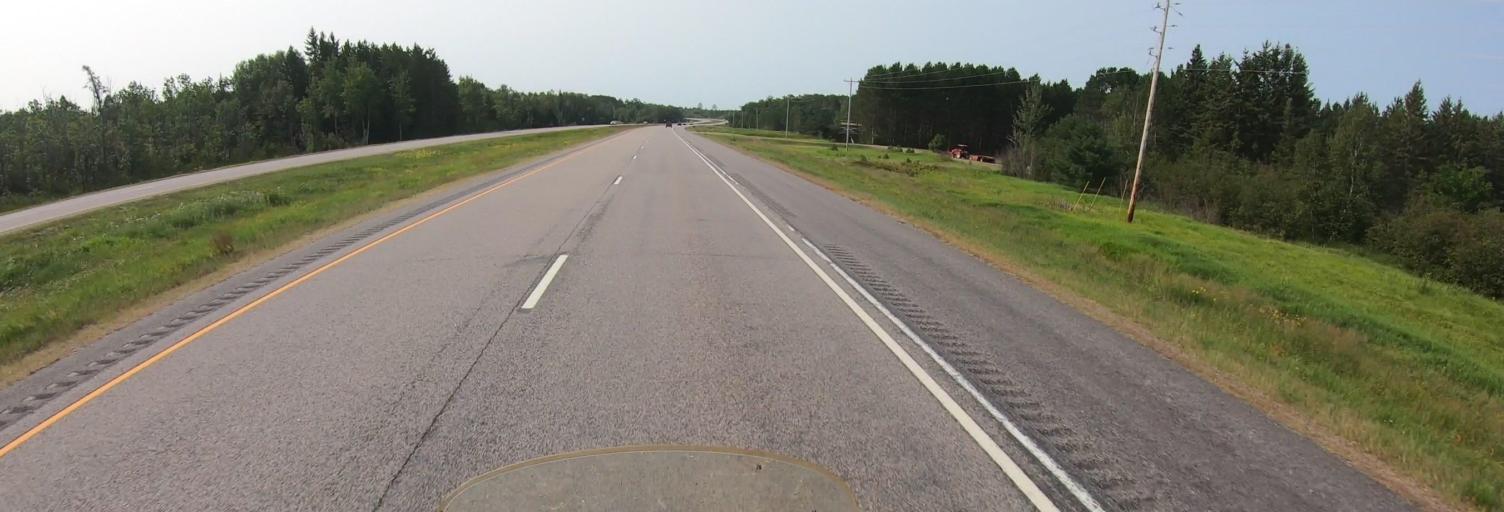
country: US
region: Minnesota
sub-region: Saint Louis County
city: Parkville
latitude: 47.6066
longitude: -92.5544
